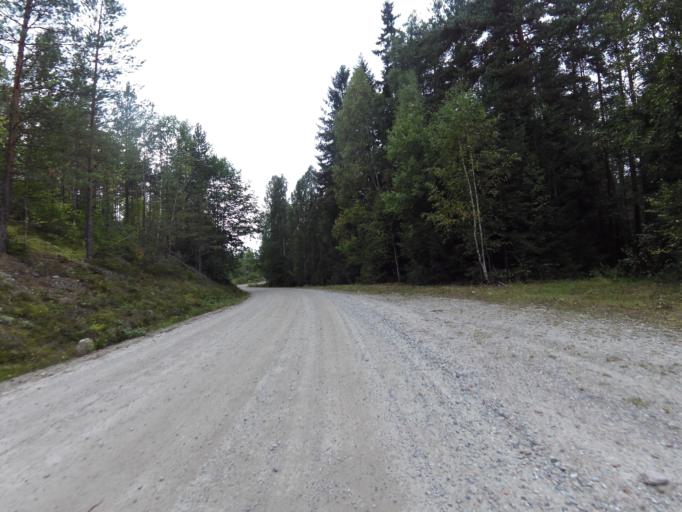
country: SE
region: Gaevleborg
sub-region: Sandvikens Kommun
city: Sandviken
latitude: 60.7640
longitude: 16.8717
